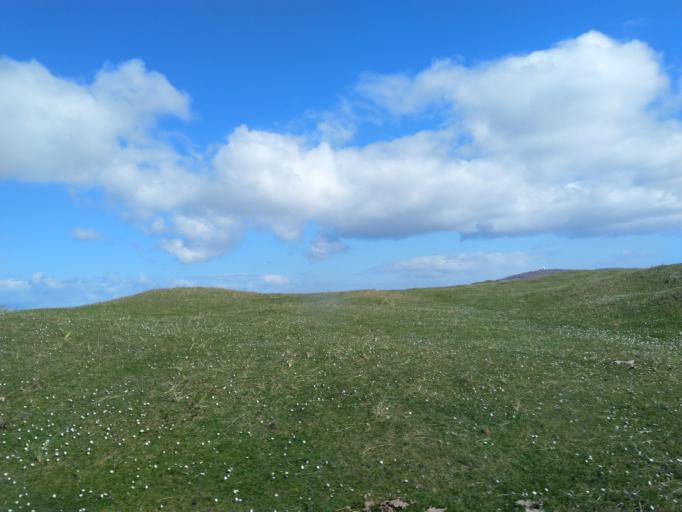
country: GB
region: Scotland
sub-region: Eilean Siar
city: Barra
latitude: 56.4789
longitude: -6.9770
